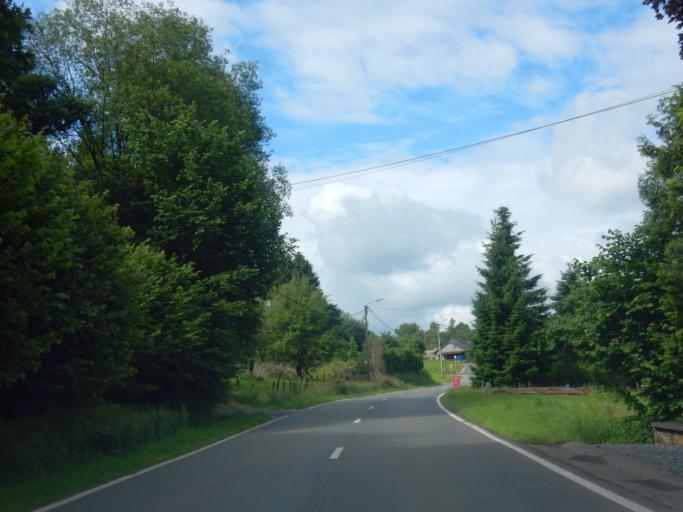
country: BE
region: Wallonia
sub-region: Province de Namur
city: Bievre
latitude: 49.8946
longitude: 5.0128
